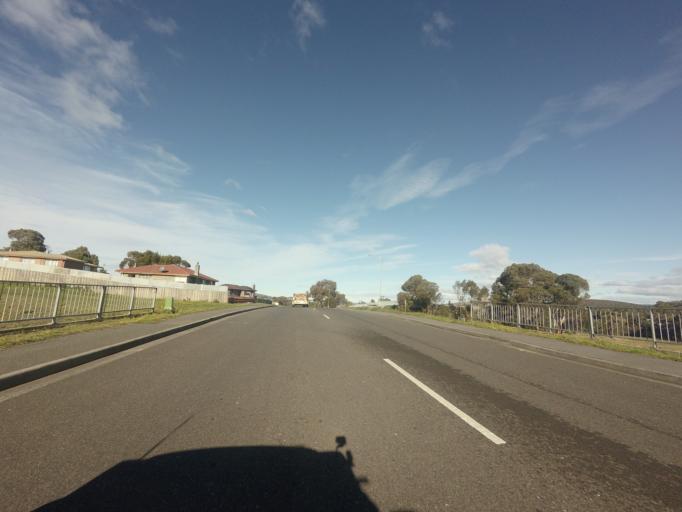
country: AU
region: Tasmania
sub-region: Clarence
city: Rokeby
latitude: -42.8910
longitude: 147.4420
